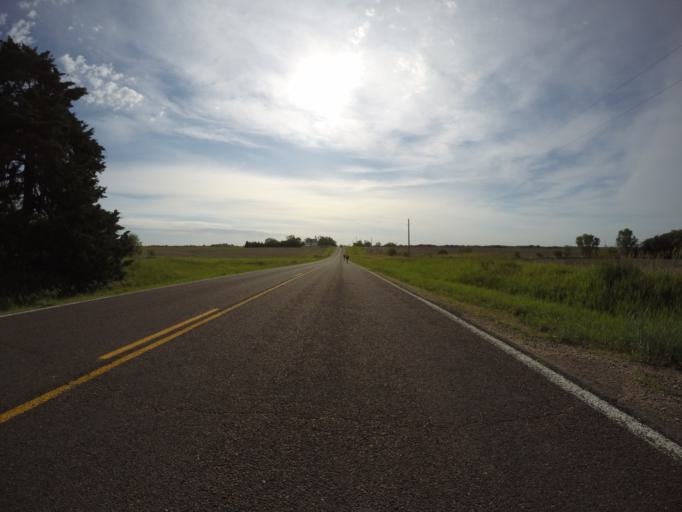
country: US
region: Kansas
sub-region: Republic County
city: Belleville
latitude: 39.7121
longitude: -97.3660
